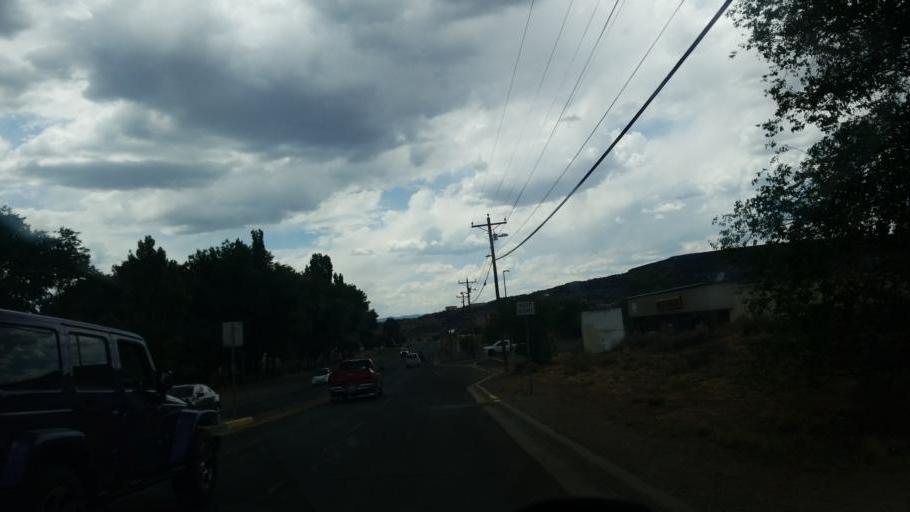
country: US
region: New Mexico
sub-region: Cibola County
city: Grants
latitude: 35.1612
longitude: -107.8350
